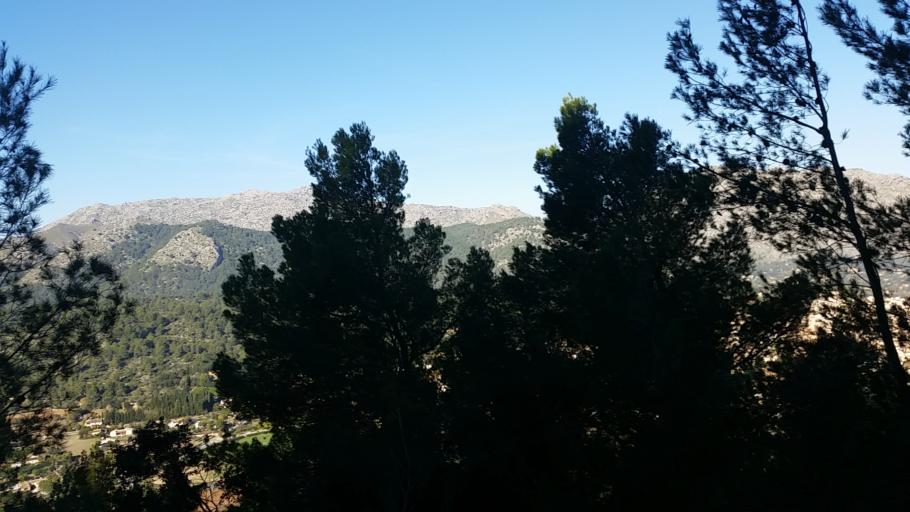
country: ES
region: Balearic Islands
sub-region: Illes Balears
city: Pollenca
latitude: 39.8680
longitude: 3.0191
